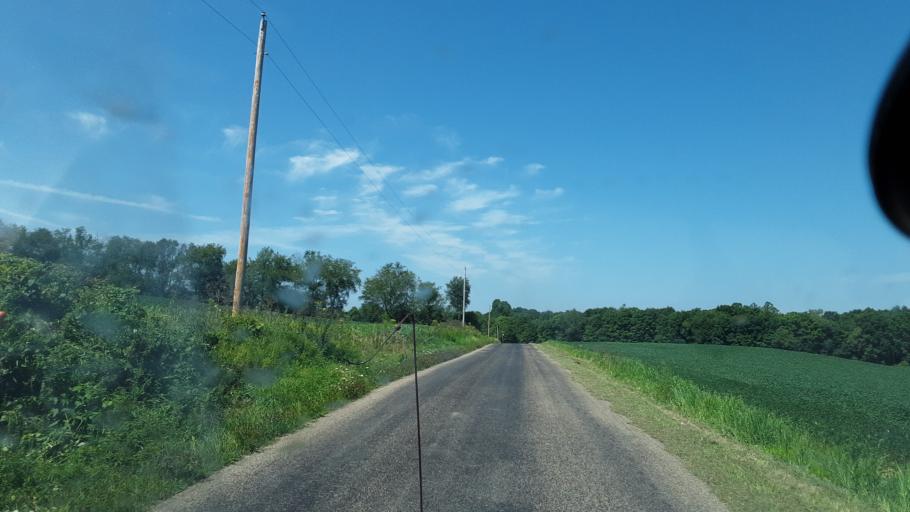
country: US
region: Ohio
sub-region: Knox County
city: Gambier
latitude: 40.3794
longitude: -82.3321
